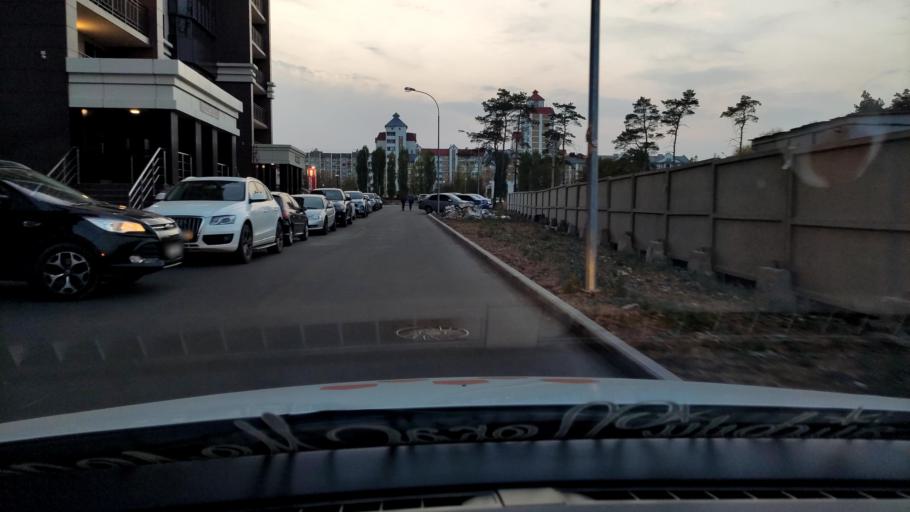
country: RU
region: Voronezj
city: Podgornoye
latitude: 51.7213
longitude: 39.1817
